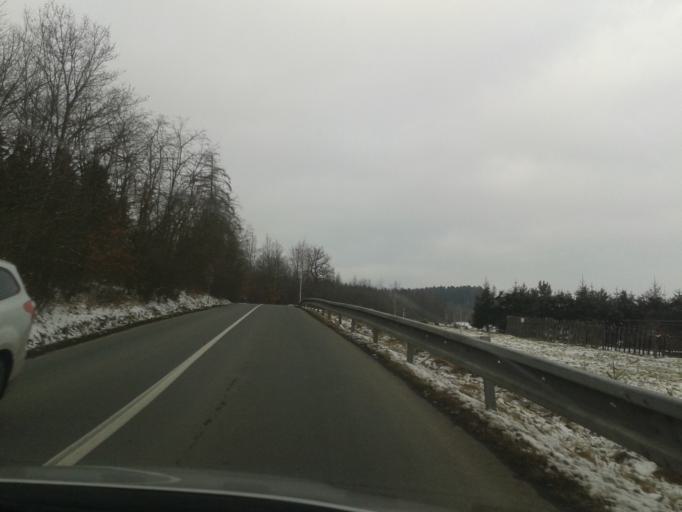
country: CZ
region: Olomoucky
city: Konice
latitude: 49.5969
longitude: 16.8896
